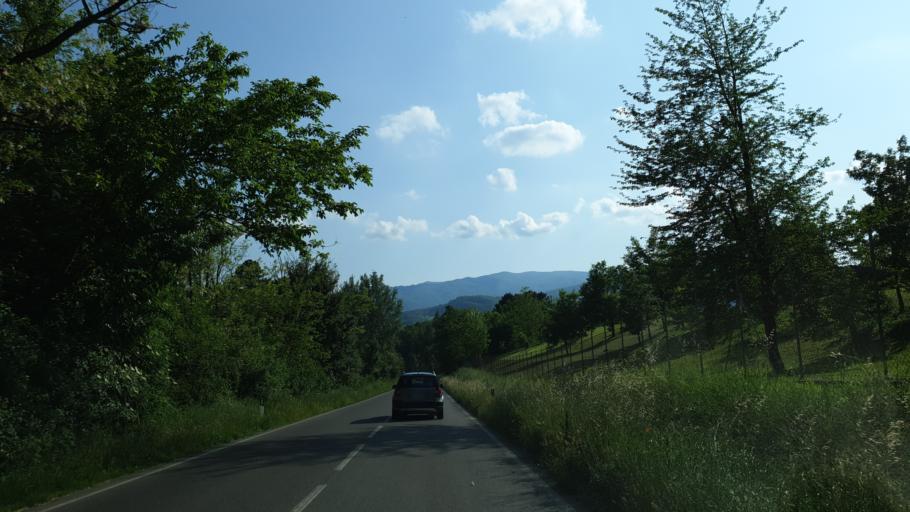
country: IT
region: Tuscany
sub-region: Province of Arezzo
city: Ponte a Poppi
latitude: 43.7288
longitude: 11.7866
